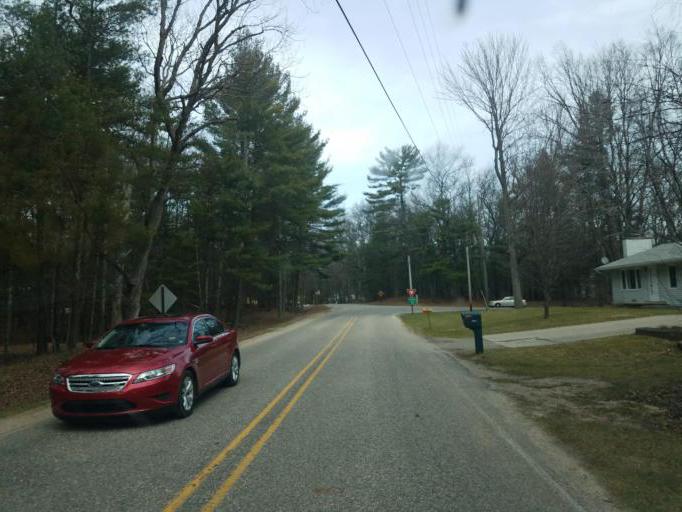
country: US
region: Michigan
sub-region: Oceana County
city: Hart
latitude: 43.7682
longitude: -86.4389
